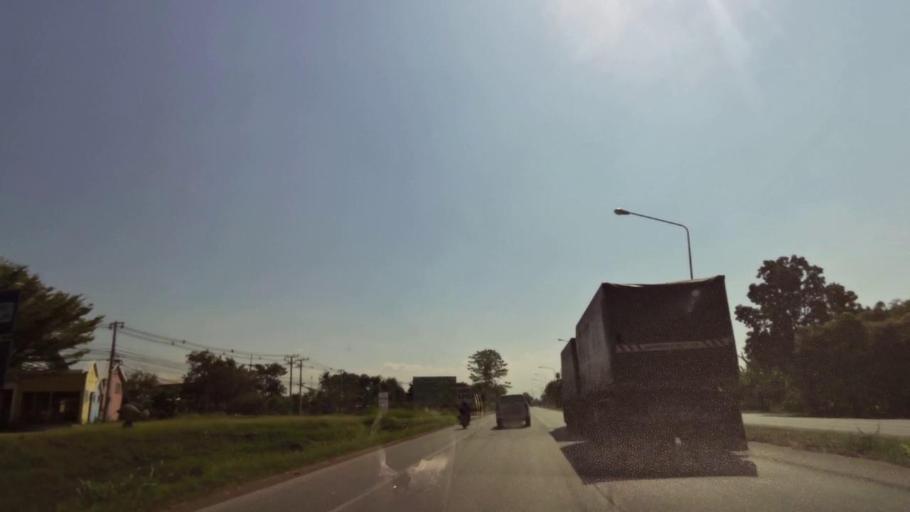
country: TH
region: Nakhon Sawan
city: Nakhon Sawan
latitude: 15.7781
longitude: 100.1213
